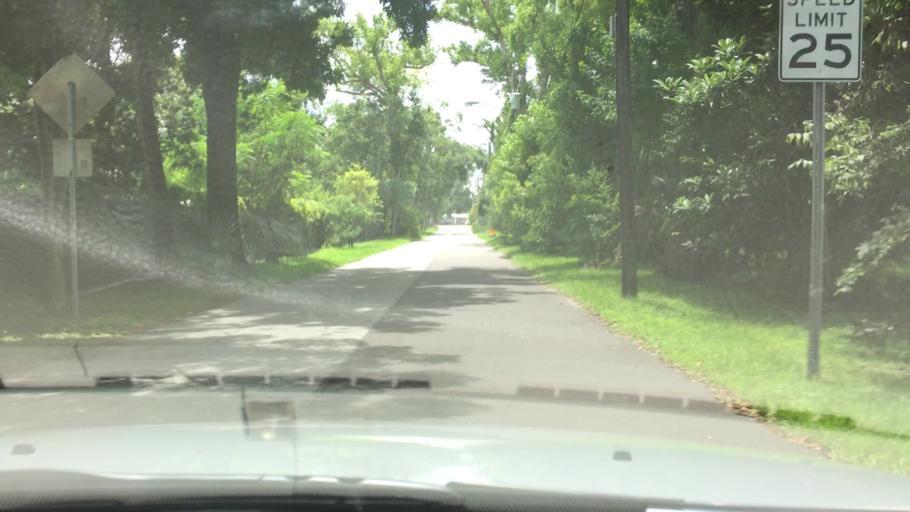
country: US
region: Florida
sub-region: Volusia County
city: Holly Hill
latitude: 29.2270
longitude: -81.0359
